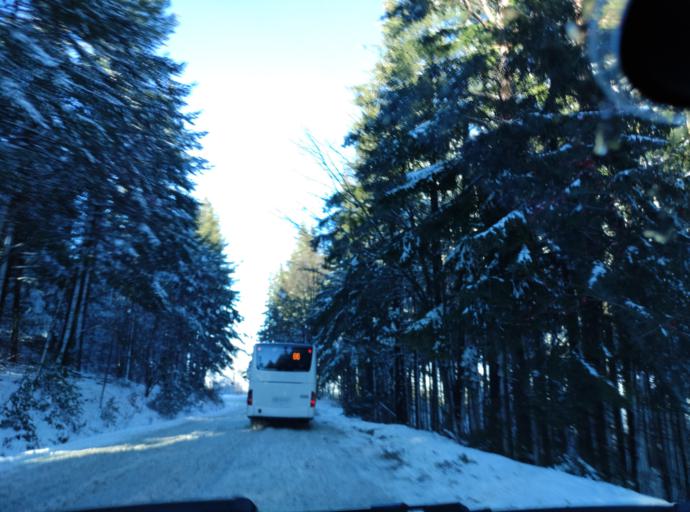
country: BG
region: Sofia-Capital
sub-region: Stolichna Obshtina
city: Sofia
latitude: 42.5933
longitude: 23.3124
